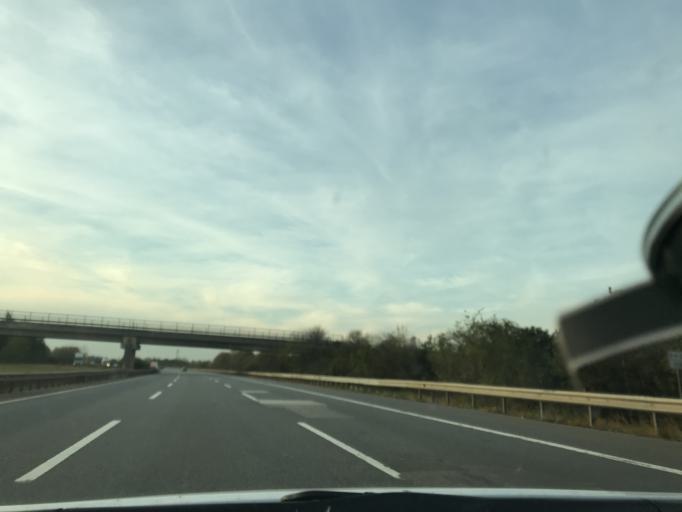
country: TR
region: Duzce
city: Cilimli
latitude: 40.8417
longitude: 31.0237
